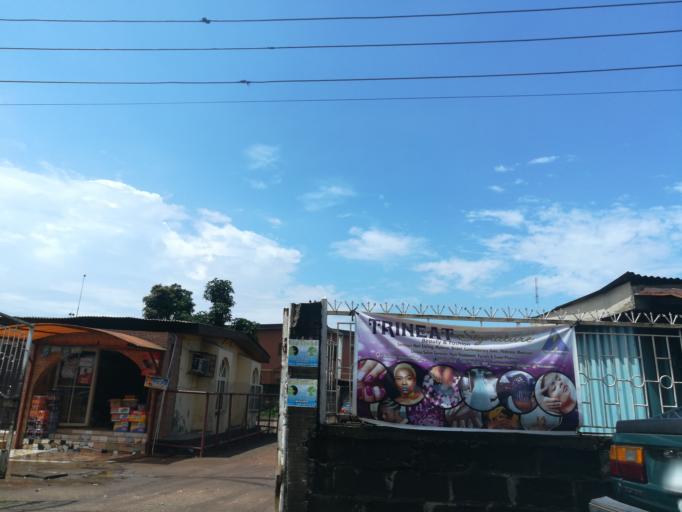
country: NG
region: Lagos
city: Somolu
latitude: 6.5604
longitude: 3.3695
